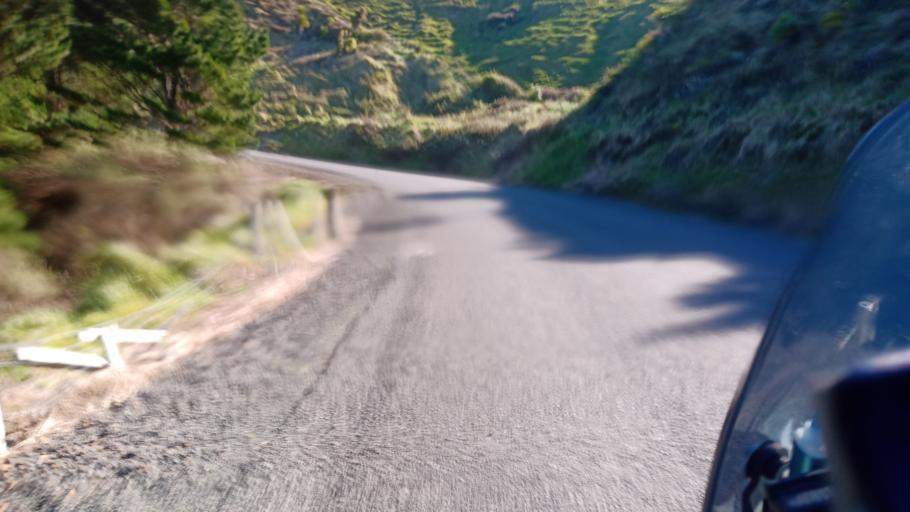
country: NZ
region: Gisborne
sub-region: Gisborne District
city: Gisborne
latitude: -39.1572
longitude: 177.9085
